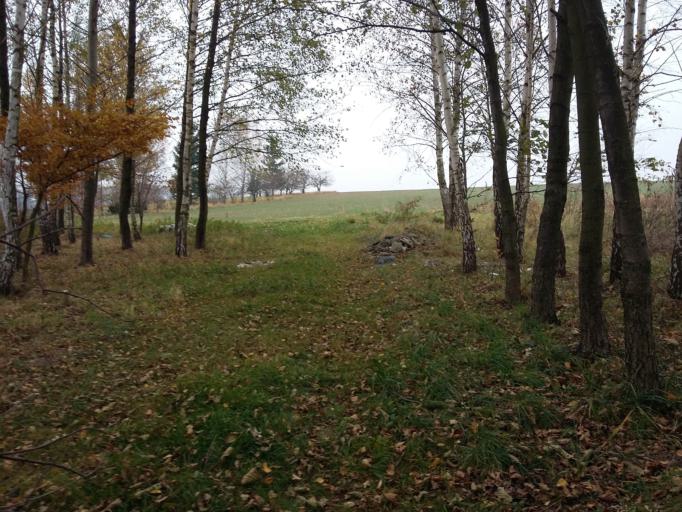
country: PL
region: Subcarpathian Voivodeship
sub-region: Powiat jasielski
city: Tarnowiec
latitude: 49.7305
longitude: 21.5682
